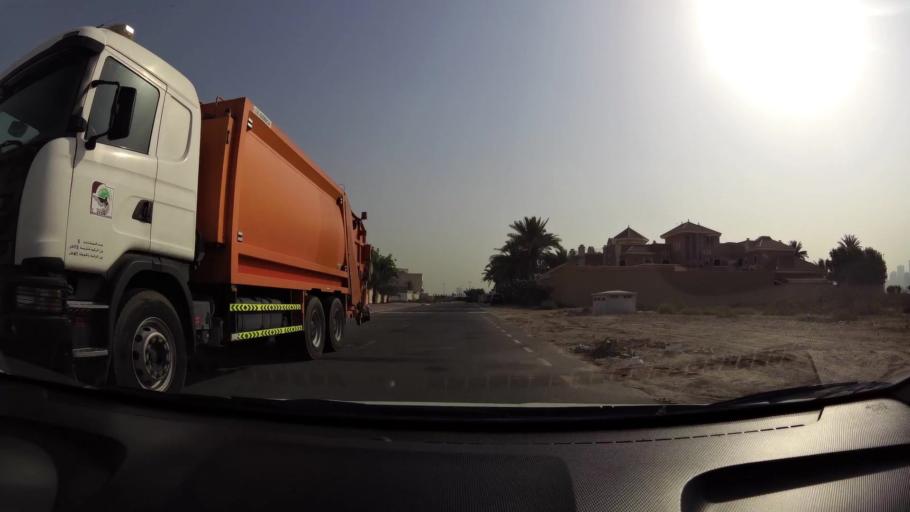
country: AE
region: Ash Shariqah
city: Sharjah
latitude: 25.3078
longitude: 55.3457
